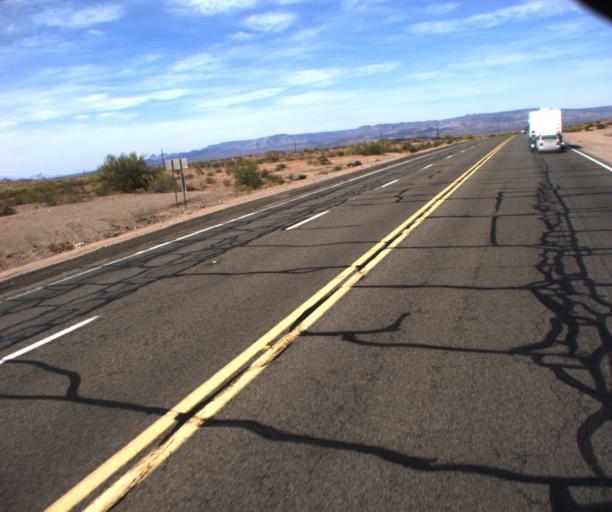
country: US
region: Arizona
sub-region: Mohave County
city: Desert Hills
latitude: 34.6476
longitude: -114.3212
